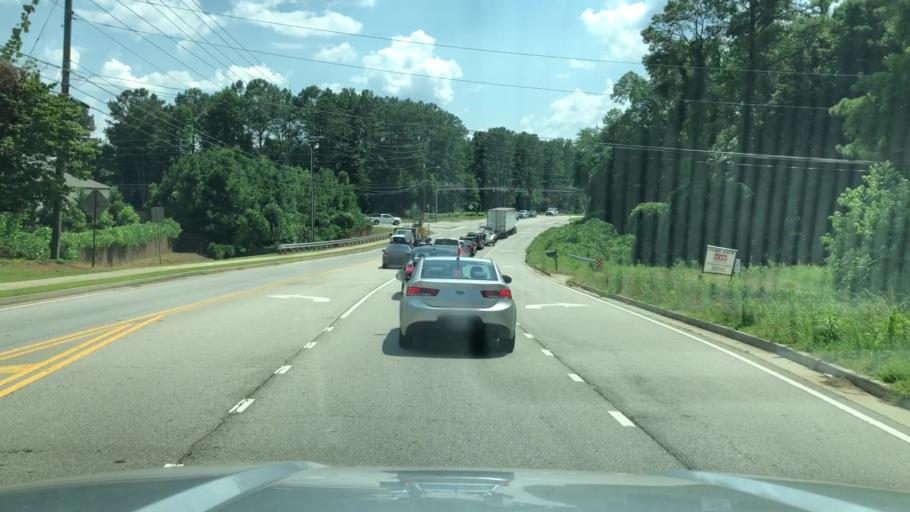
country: US
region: Georgia
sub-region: Cobb County
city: Acworth
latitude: 33.9923
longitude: -84.7084
